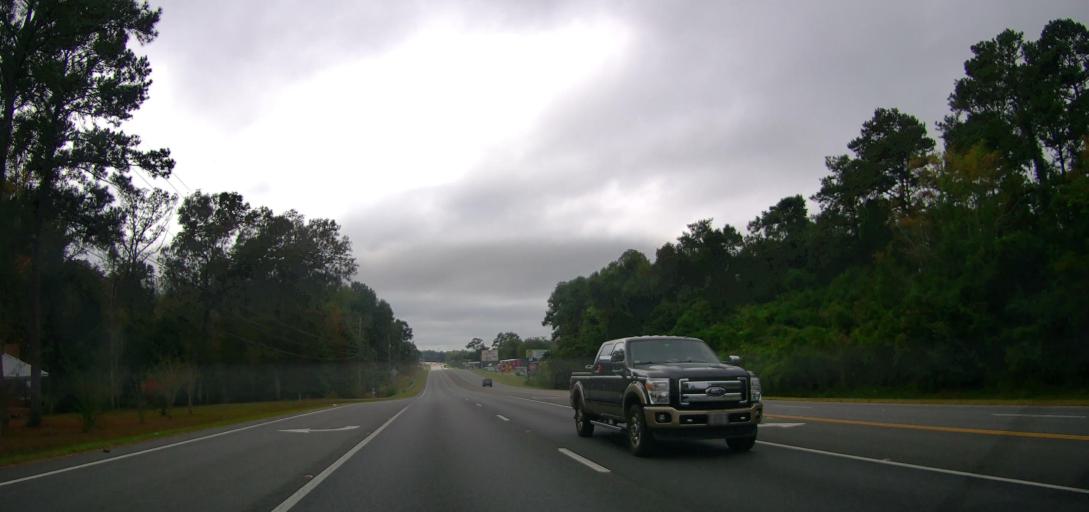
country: US
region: Georgia
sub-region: Thomas County
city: Thomasville
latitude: 30.8790
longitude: -83.9325
